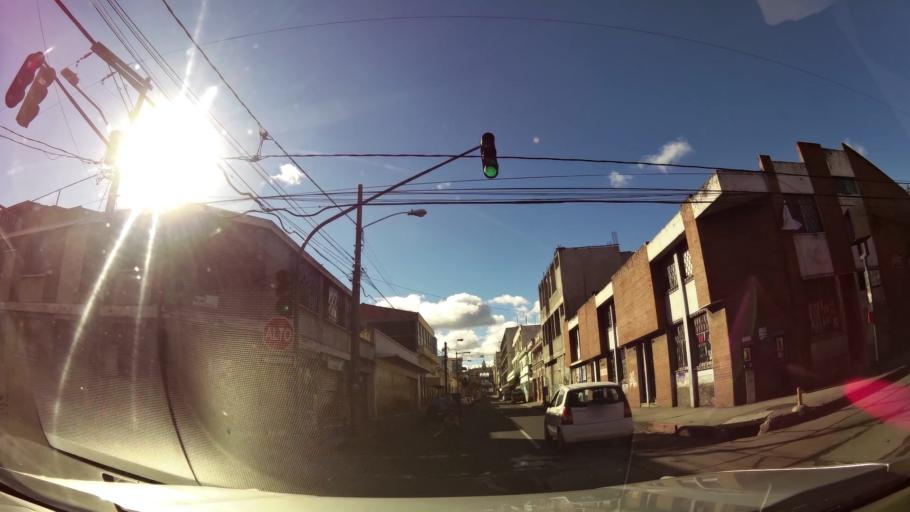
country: GT
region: Guatemala
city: Guatemala City
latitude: 14.6366
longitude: -90.5101
